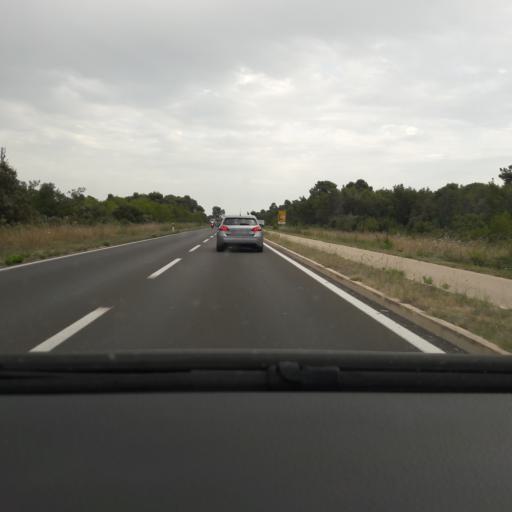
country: HR
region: Zadarska
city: Nin
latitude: 44.1797
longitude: 15.1880
